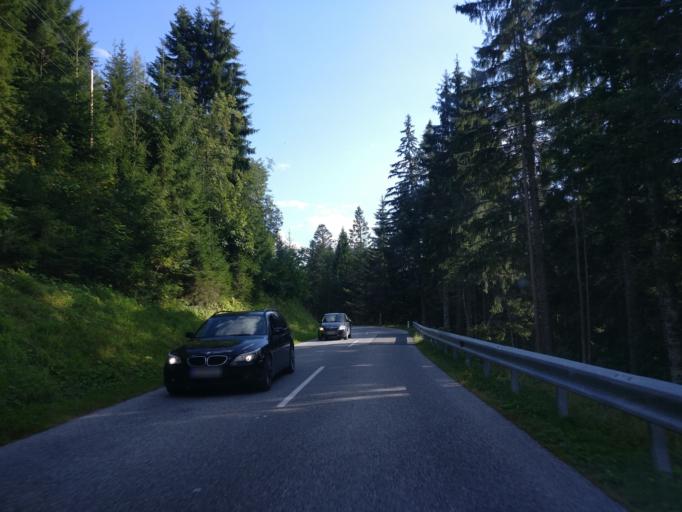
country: AT
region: Salzburg
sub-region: Politischer Bezirk Sankt Johann im Pongau
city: Muhlbach am Hochkonig
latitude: 47.3960
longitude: 13.1144
